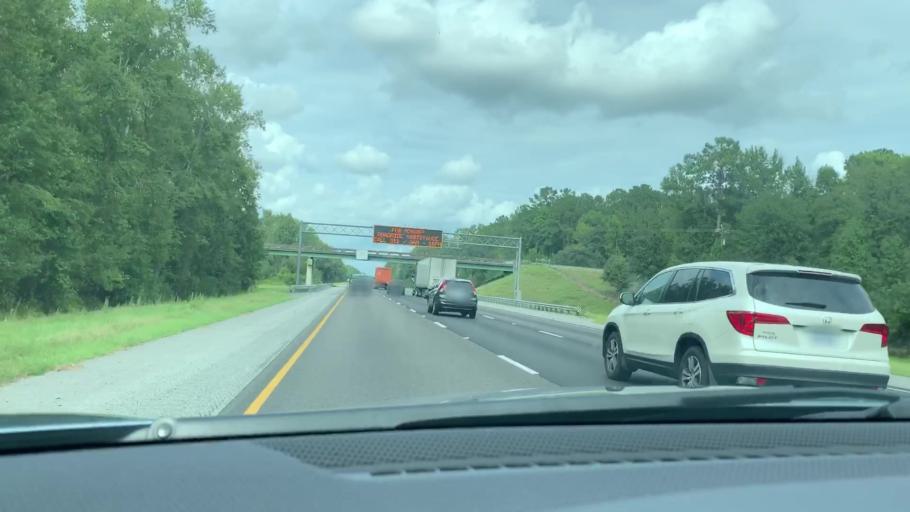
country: US
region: Georgia
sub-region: Liberty County
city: Midway
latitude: 31.6944
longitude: -81.3911
